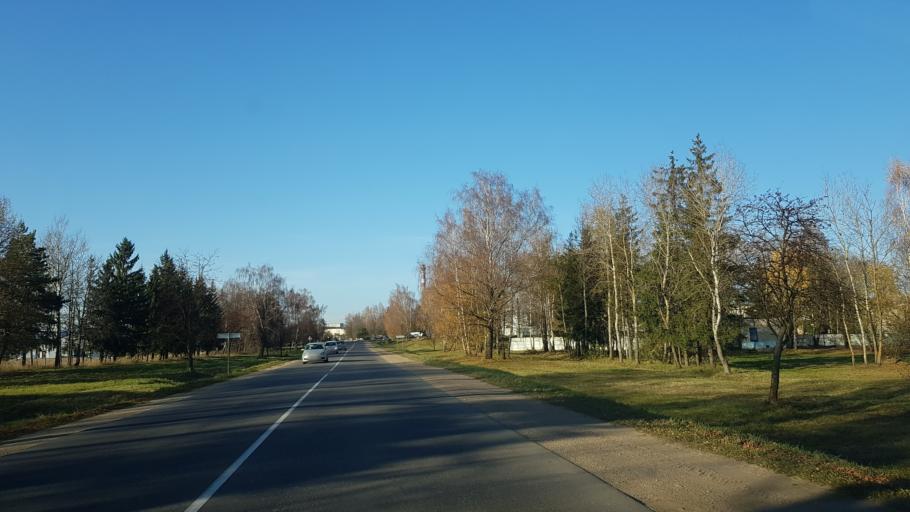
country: BY
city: Fanipol
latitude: 53.7309
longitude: 27.3328
